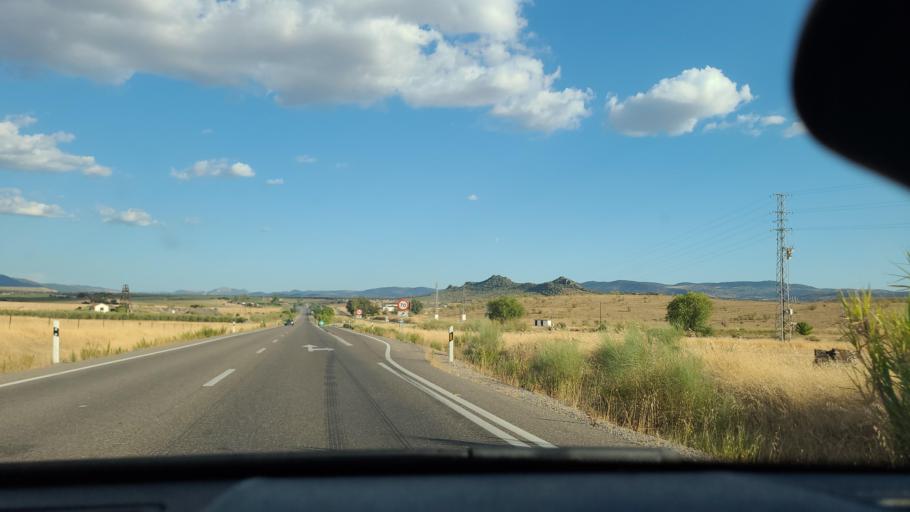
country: ES
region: Andalusia
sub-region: Province of Cordoba
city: Belmez
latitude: 38.2741
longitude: -5.1967
